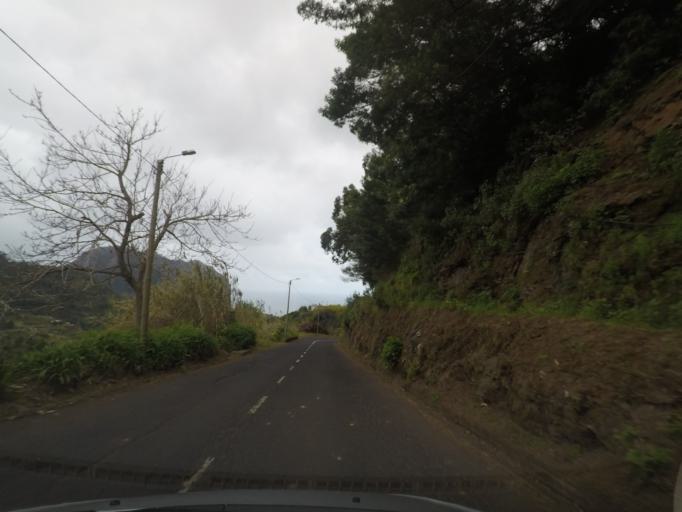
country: PT
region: Madeira
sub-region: Santana
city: Santana
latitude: 32.7519
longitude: -16.8386
